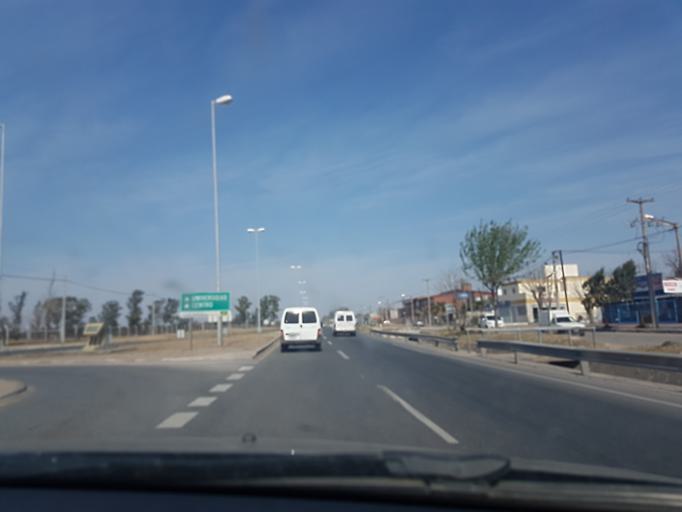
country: AR
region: Cordoba
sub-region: Departamento de Capital
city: Cordoba
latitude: -31.4859
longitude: -64.2463
